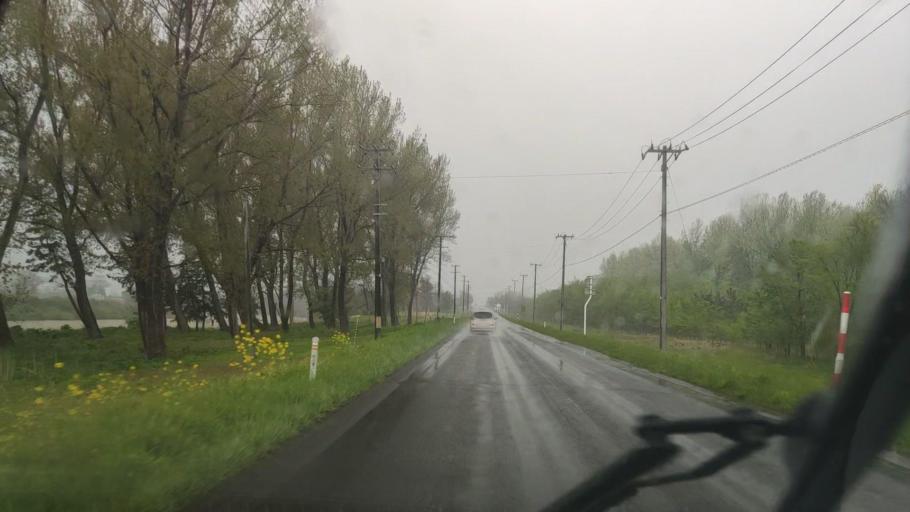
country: JP
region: Akita
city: Tenno
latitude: 39.9478
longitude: 139.9459
